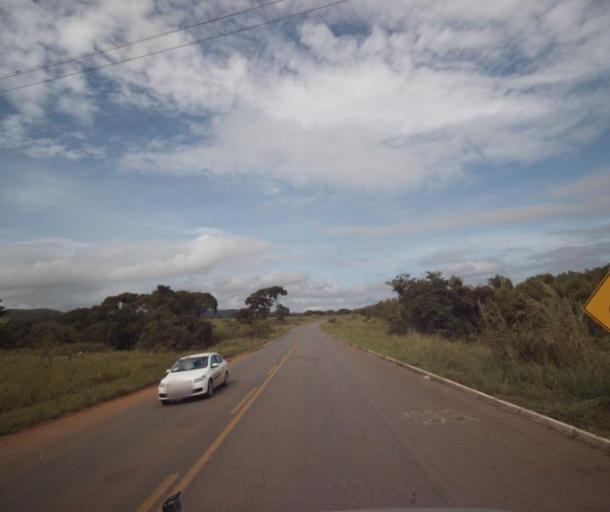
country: BR
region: Goias
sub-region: Pirenopolis
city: Pirenopolis
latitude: -15.6677
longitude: -48.6913
